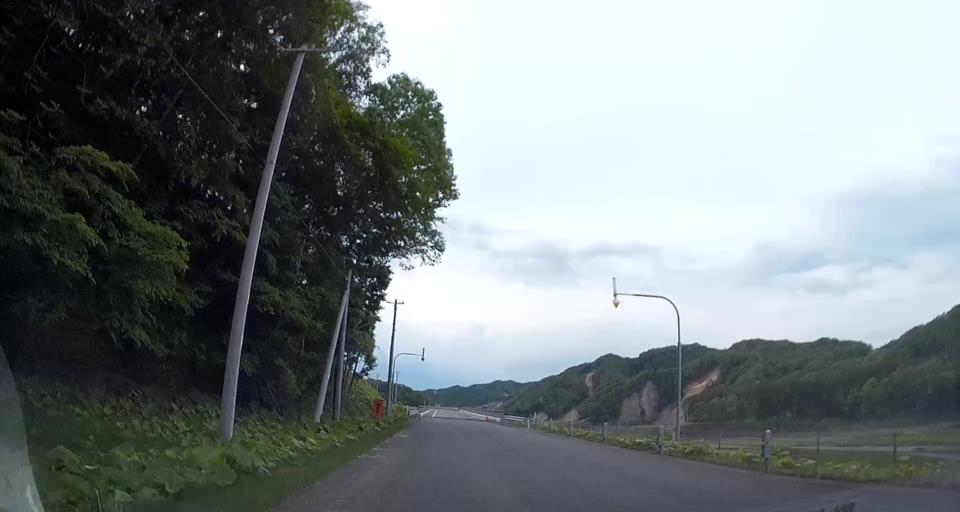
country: JP
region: Hokkaido
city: Chitose
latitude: 42.7861
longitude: 142.0254
